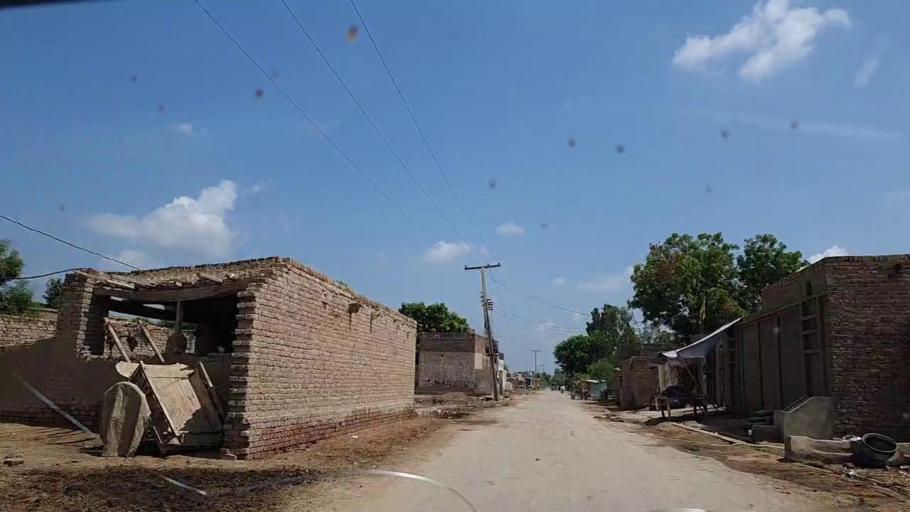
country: PK
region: Sindh
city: Tharu Shah
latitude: 26.9600
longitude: 68.1005
